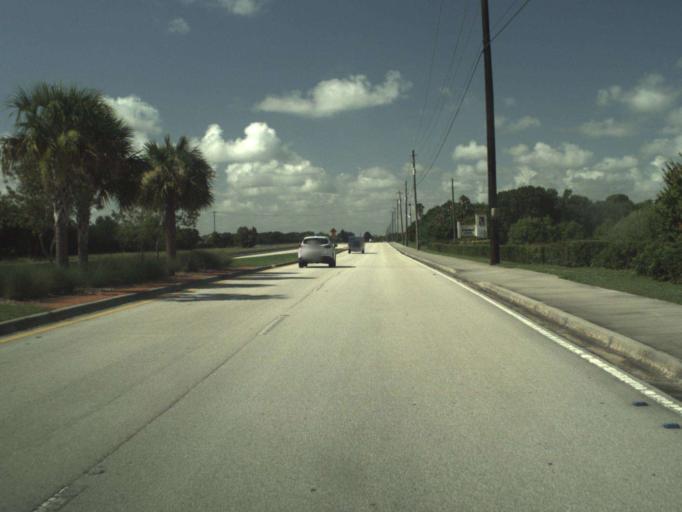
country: US
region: Florida
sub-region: Indian River County
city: Vero Beach South
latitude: 27.5984
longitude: -80.4474
